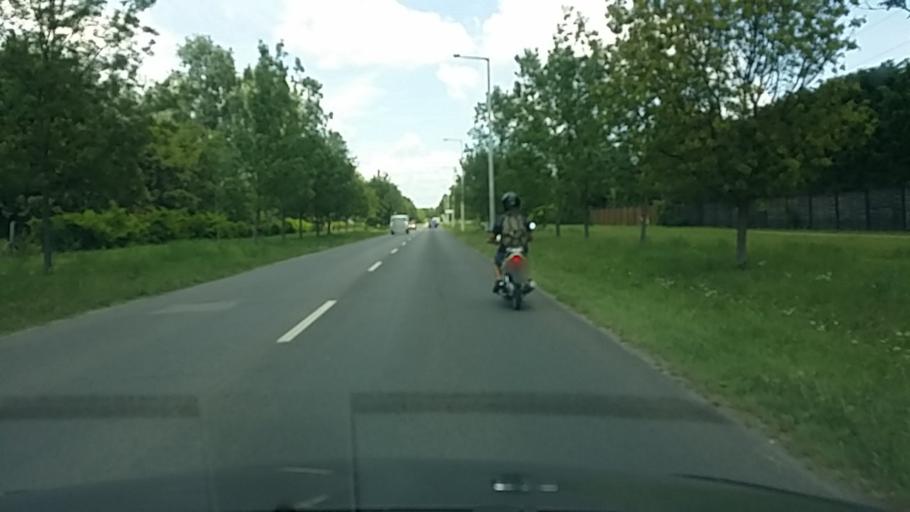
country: HU
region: Bacs-Kiskun
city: Kecskemet
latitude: 46.9134
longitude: 19.6558
